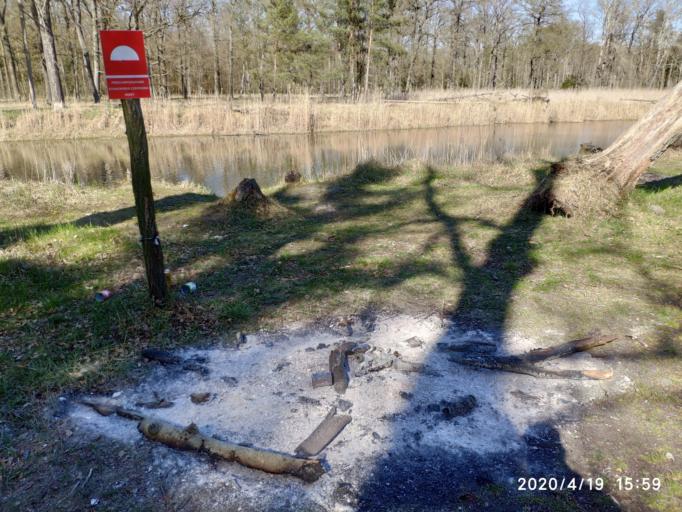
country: PL
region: Lubusz
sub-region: Powiat zielonogorski
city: Zabor
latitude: 51.9799
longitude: 15.6761
